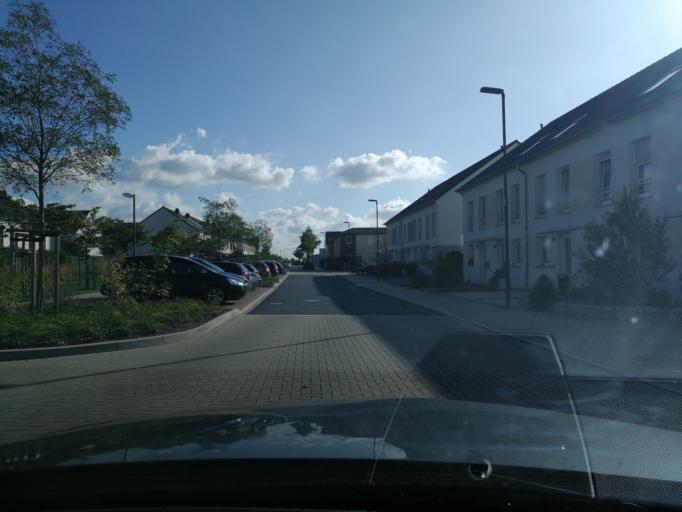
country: DE
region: North Rhine-Westphalia
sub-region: Regierungsbezirk Dusseldorf
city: Dusseldorf
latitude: 51.1427
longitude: 6.7505
